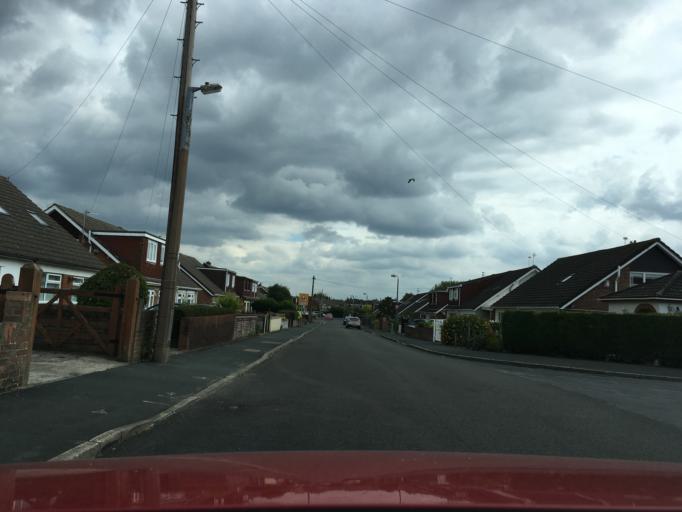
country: GB
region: England
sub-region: South Gloucestershire
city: Almondsbury
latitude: 51.5345
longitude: -2.5601
